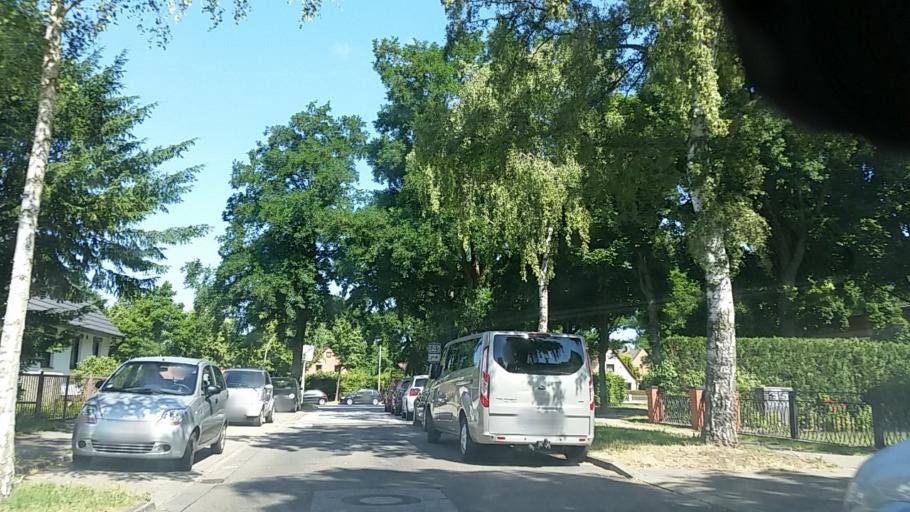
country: DE
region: Schleswig-Holstein
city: Oststeinbek
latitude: 53.5405
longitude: 10.1378
